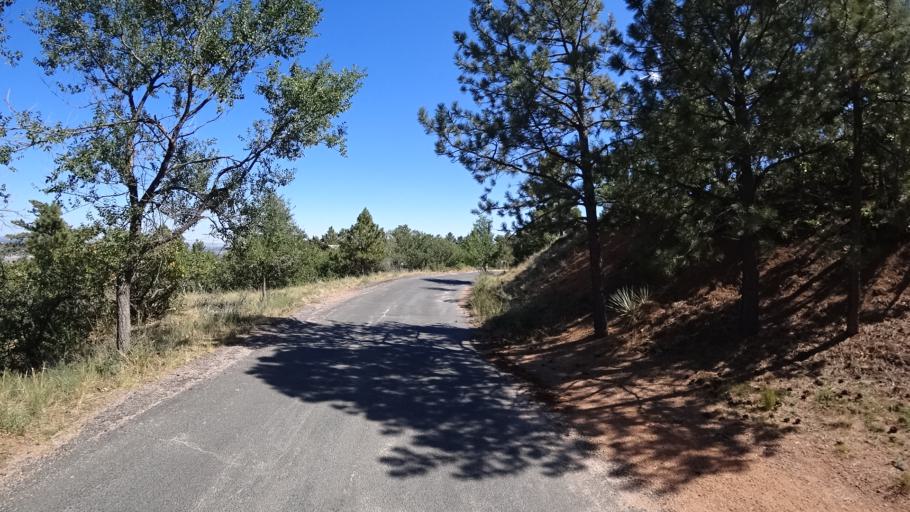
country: US
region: Colorado
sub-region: El Paso County
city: Colorado Springs
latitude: 38.8148
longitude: -104.8758
